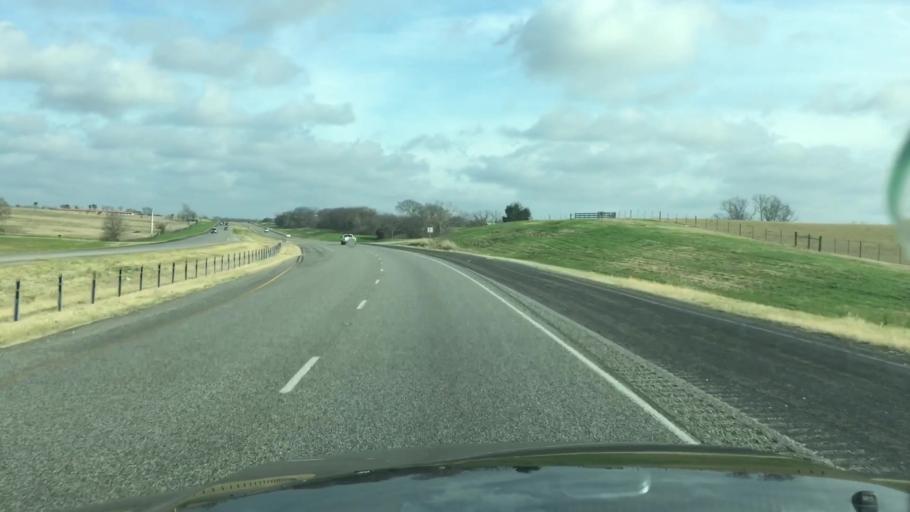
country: US
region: Texas
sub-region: Washington County
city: Brenham
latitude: 30.1374
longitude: -96.3497
